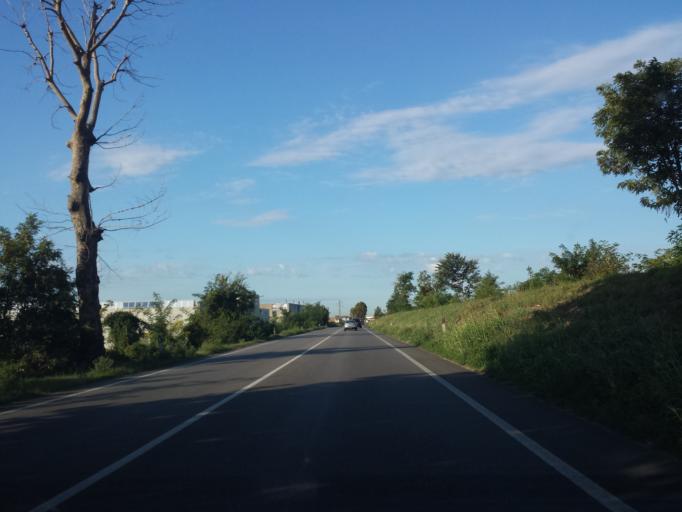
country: IT
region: Veneto
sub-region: Provincia di Vicenza
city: Montebello Vicentino
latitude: 45.4493
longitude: 11.3822
